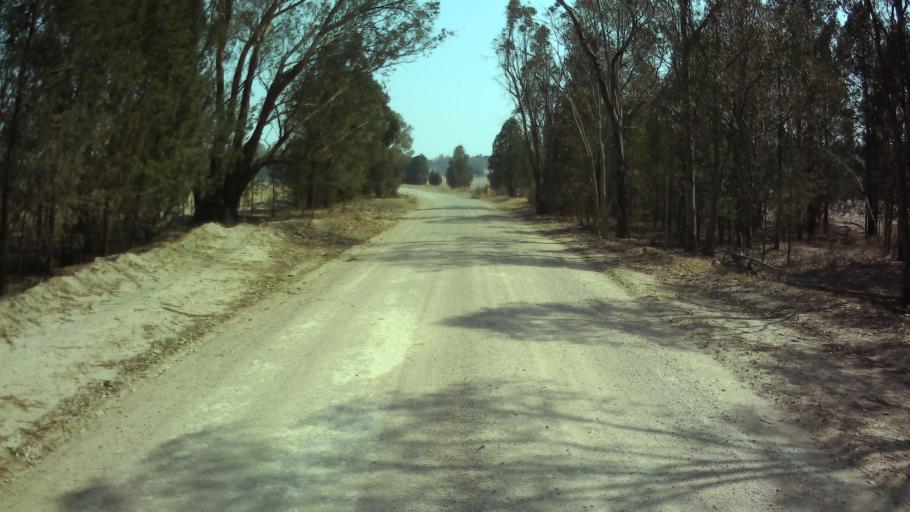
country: AU
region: New South Wales
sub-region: Weddin
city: Grenfell
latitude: -33.6713
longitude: 148.2749
